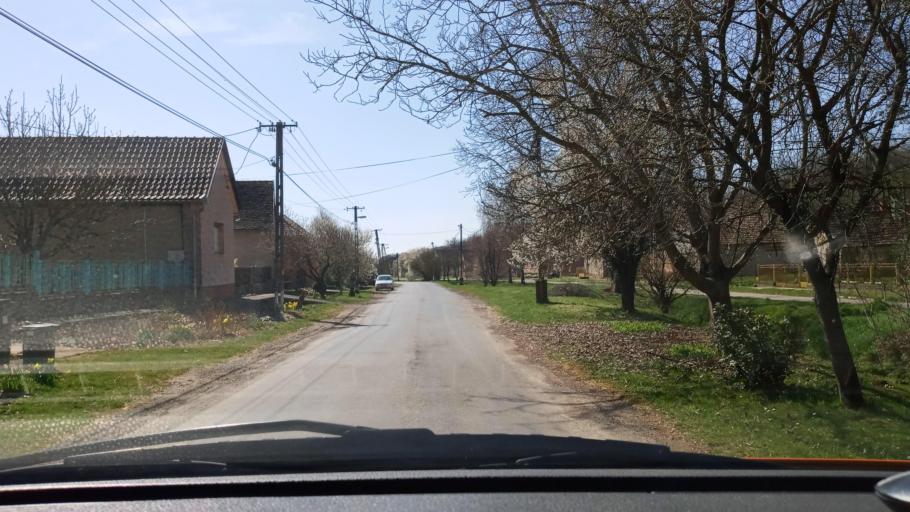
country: HU
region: Baranya
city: Pecsvarad
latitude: 46.0655
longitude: 18.4494
